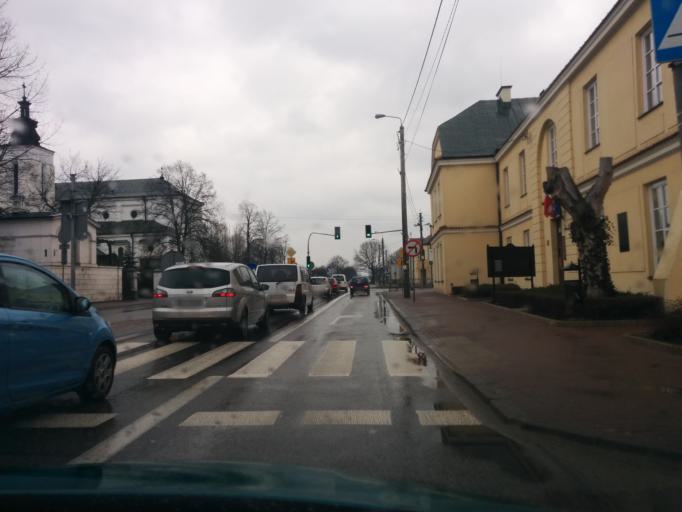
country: PL
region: Masovian Voivodeship
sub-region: Powiat legionowski
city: Jablonna
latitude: 52.3776
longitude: 20.9180
